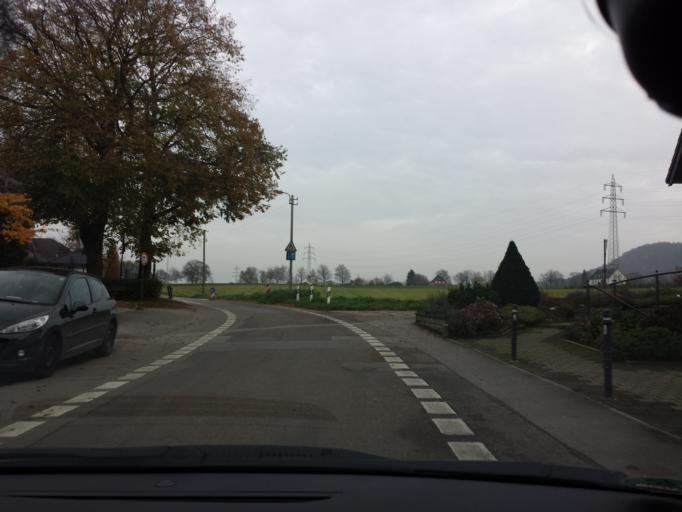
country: DE
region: North Rhine-Westphalia
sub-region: Regierungsbezirk Koln
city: Herzogenrath
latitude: 50.8913
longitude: 6.0923
